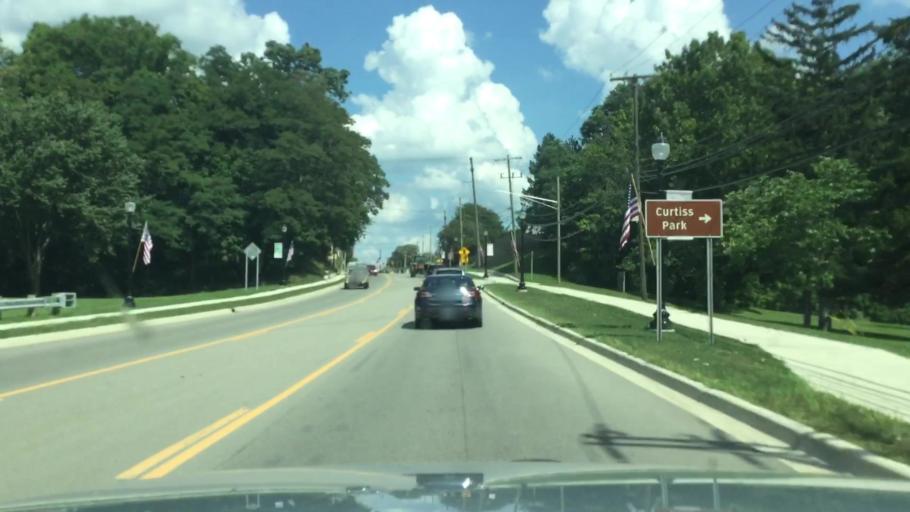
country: US
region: Michigan
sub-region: Washtenaw County
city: Saline
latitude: 42.1635
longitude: -83.7888
